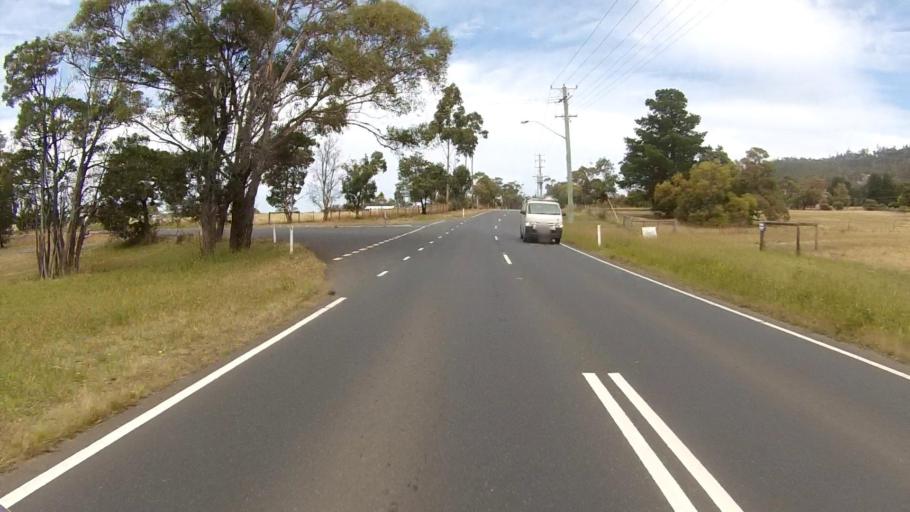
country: AU
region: Tasmania
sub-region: Clarence
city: Acton Park
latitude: -42.8877
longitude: 147.4830
